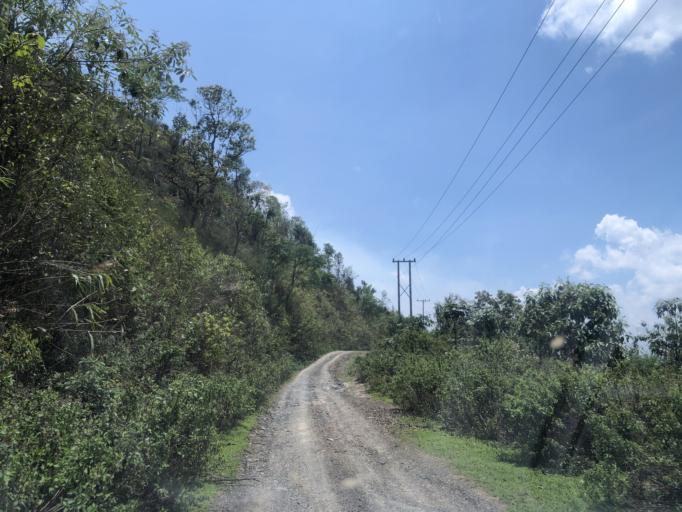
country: LA
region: Phongsali
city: Phongsali
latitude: 21.4378
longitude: 102.1621
